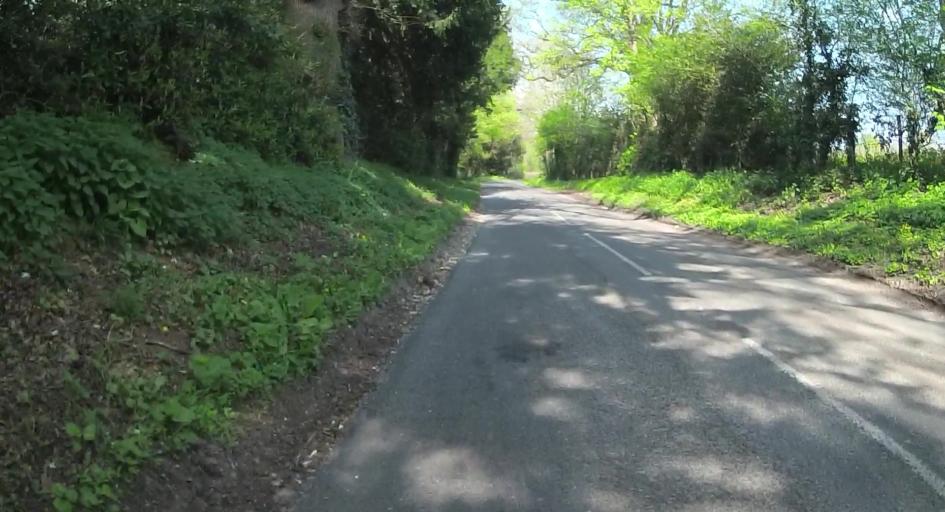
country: GB
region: England
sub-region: Hampshire
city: Basingstoke
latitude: 51.3036
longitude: -1.0885
